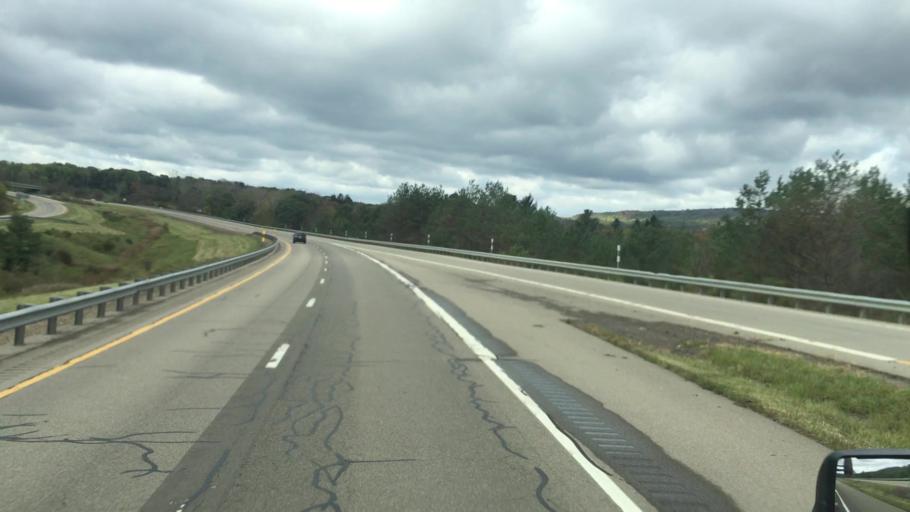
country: US
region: New York
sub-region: Allegany County
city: Belmont
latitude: 42.3013
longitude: -78.0163
